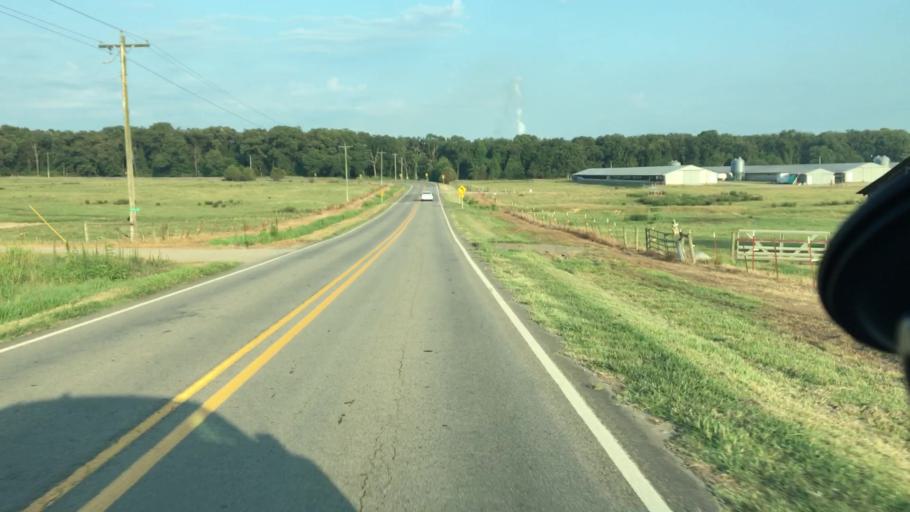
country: US
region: Arkansas
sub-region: Johnson County
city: Clarksville
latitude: 35.3794
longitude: -93.5565
